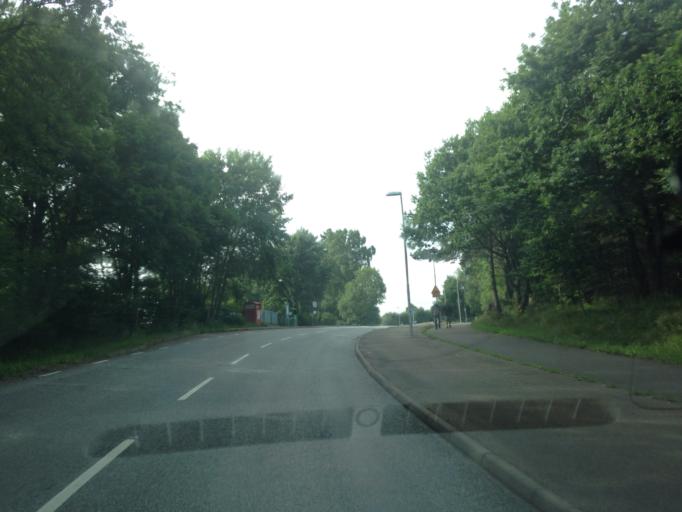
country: SE
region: Vaestra Goetaland
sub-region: Goteborg
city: Goeteborg
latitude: 57.7568
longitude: 11.9684
